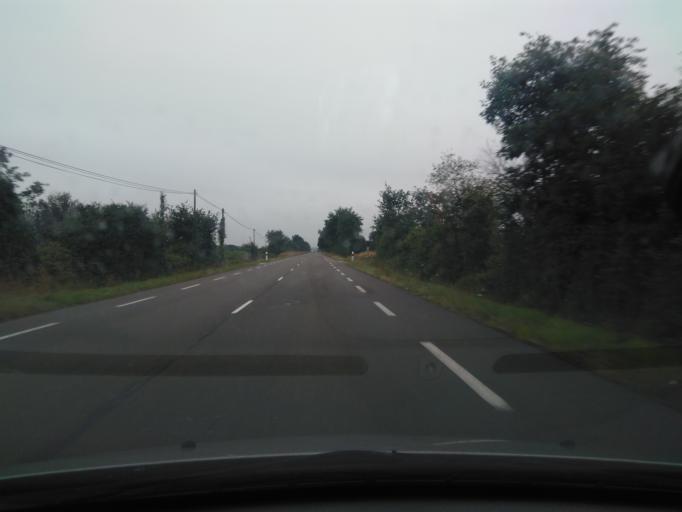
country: FR
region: Pays de la Loire
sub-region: Departement de la Vendee
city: Saint-Georges-de-Pointindoux
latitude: 46.6275
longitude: -1.6243
